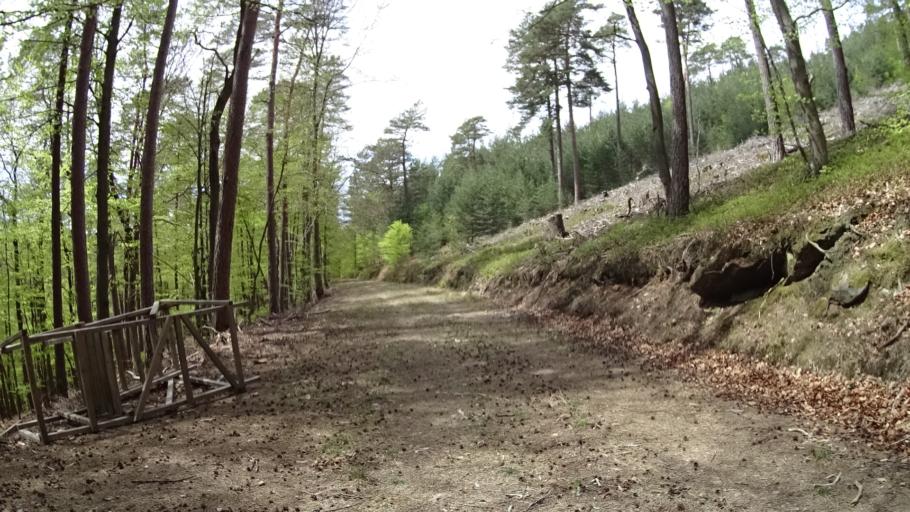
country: DE
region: Rheinland-Pfalz
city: Ramberg
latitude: 49.3138
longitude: 8.0113
